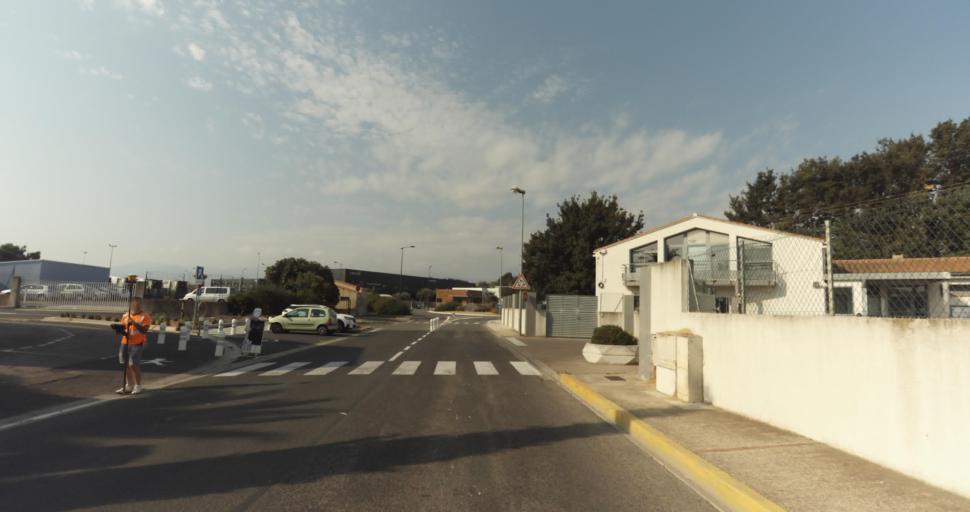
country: FR
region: Languedoc-Roussillon
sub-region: Departement des Pyrenees-Orientales
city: Latour-Bas-Elne
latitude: 42.6149
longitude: 2.9942
